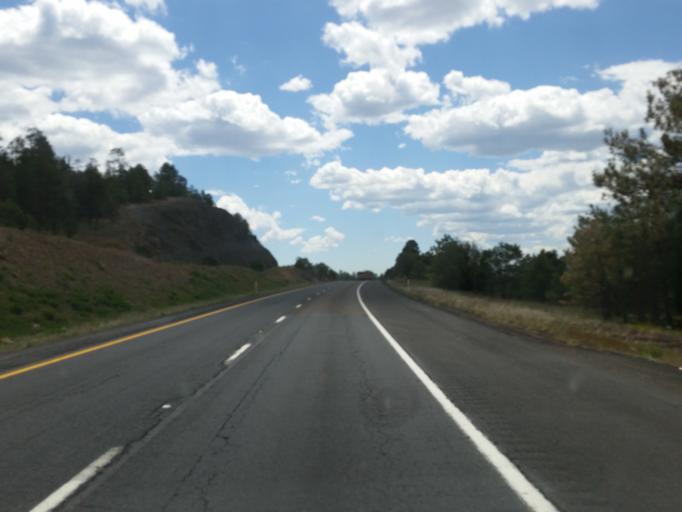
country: US
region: Arizona
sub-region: Coconino County
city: Parks
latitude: 35.2507
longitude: -111.8971
